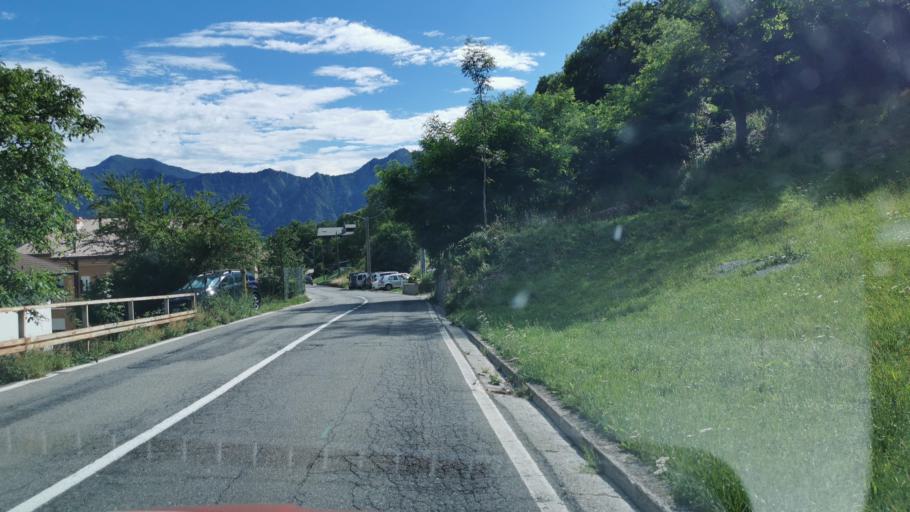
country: IT
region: Lombardy
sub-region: Provincia di Lecco
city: Casargo
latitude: 46.0417
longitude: 9.3883
